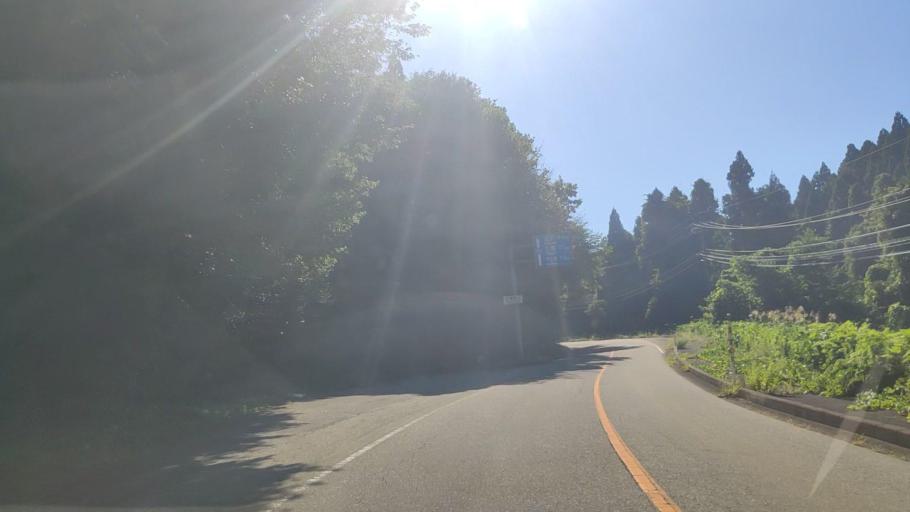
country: JP
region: Ishikawa
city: Nanao
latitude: 37.3464
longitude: 137.2293
